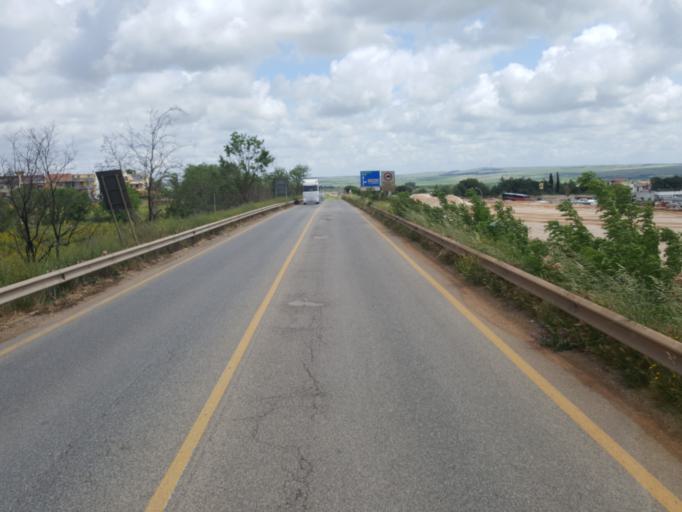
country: IT
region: Apulia
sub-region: Provincia di Bari
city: Altamura
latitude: 40.8153
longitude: 16.5632
